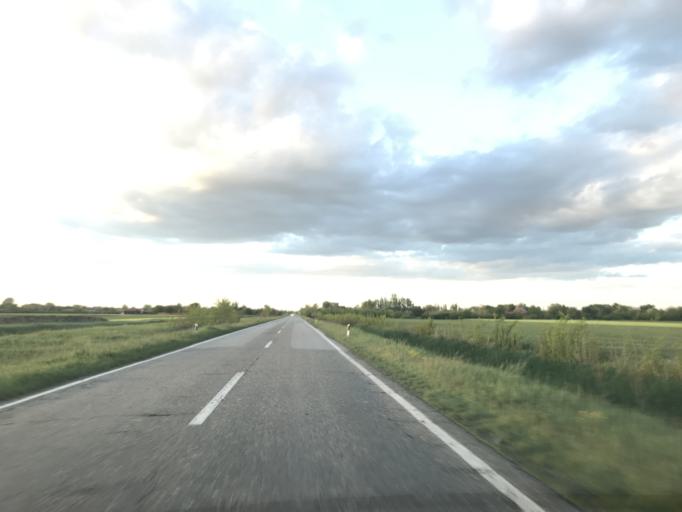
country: RS
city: Banatsko Karadordevo
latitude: 45.5804
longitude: 20.5482
